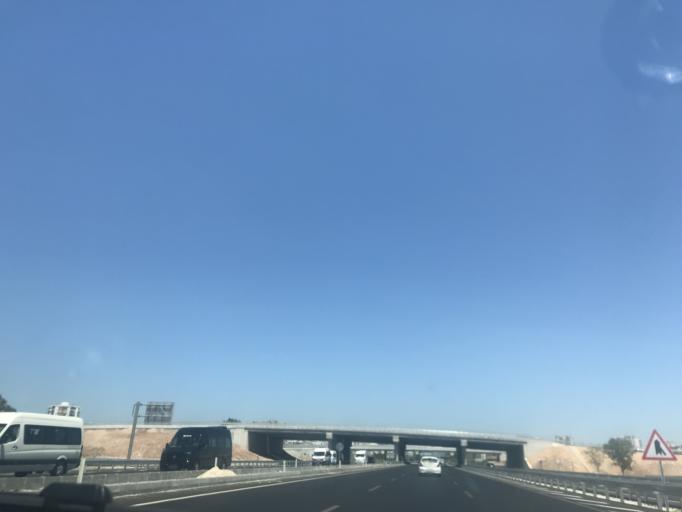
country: TR
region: Antalya
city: Cakirlar
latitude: 36.8456
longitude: 30.6000
